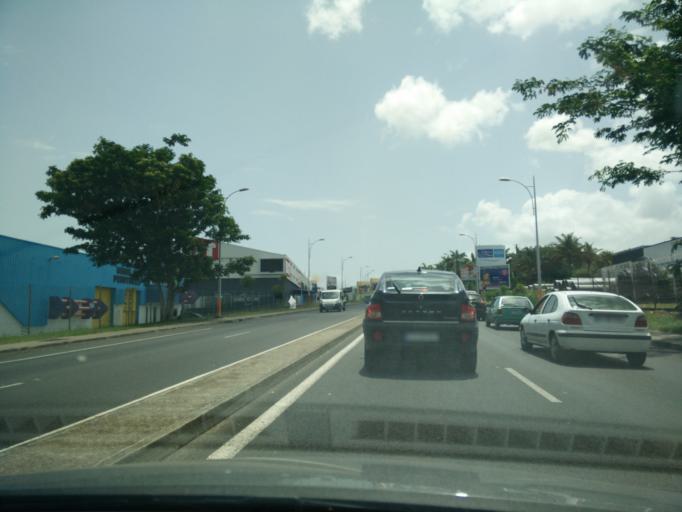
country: GP
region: Guadeloupe
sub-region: Guadeloupe
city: Baie-Mahault
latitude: 16.2404
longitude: -61.5802
